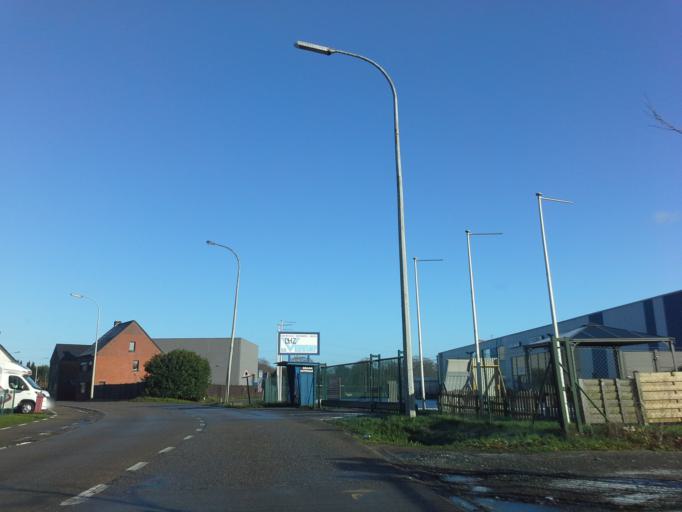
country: BE
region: Flanders
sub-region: Provincie Antwerpen
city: Herentals
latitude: 51.1673
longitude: 4.7978
